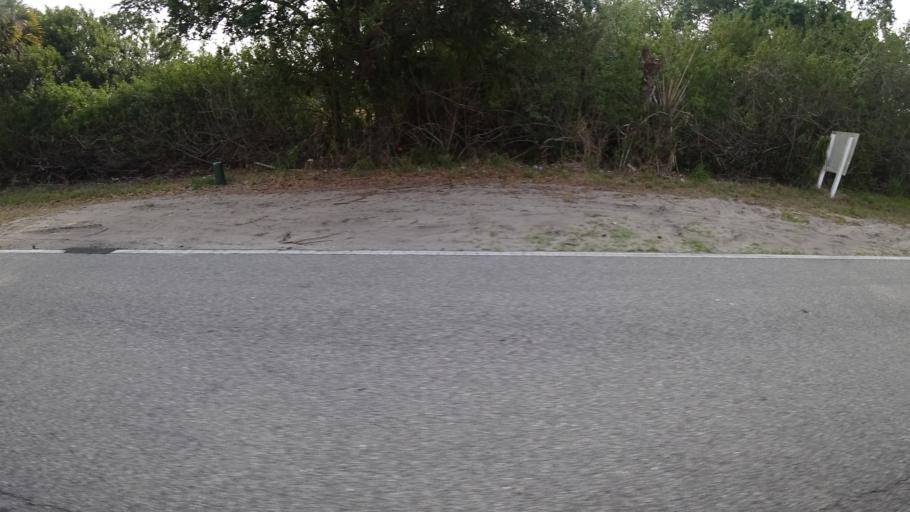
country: US
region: Florida
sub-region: Manatee County
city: Whitfield
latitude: 27.4231
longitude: -82.5219
